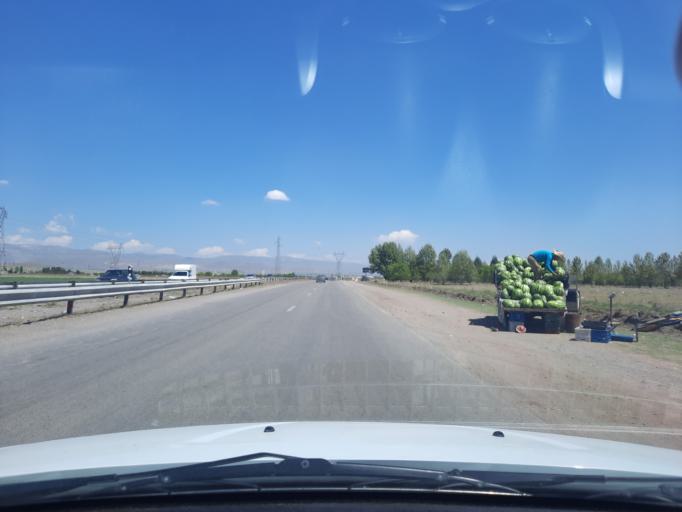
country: IR
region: Qazvin
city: Qazvin
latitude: 36.2672
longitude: 50.0798
